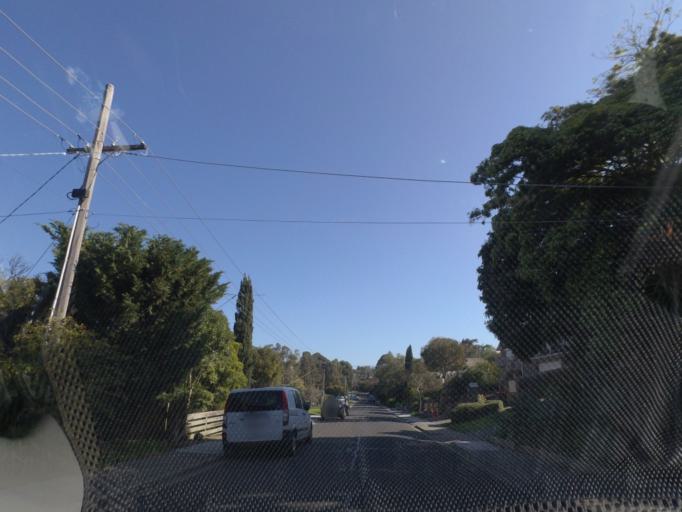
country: AU
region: Victoria
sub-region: Whitehorse
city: Mont Albert North
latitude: -37.7950
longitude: 145.1056
